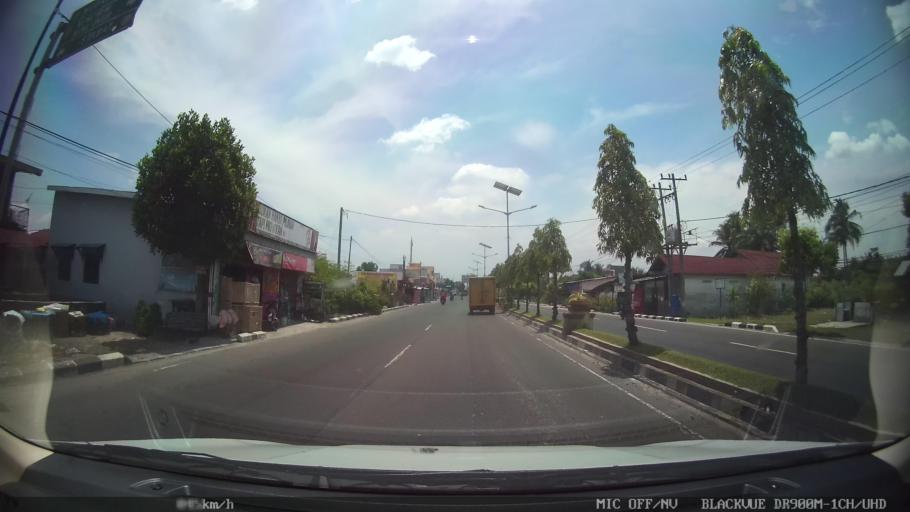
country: ID
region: North Sumatra
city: Binjai
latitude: 3.6085
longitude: 98.5152
